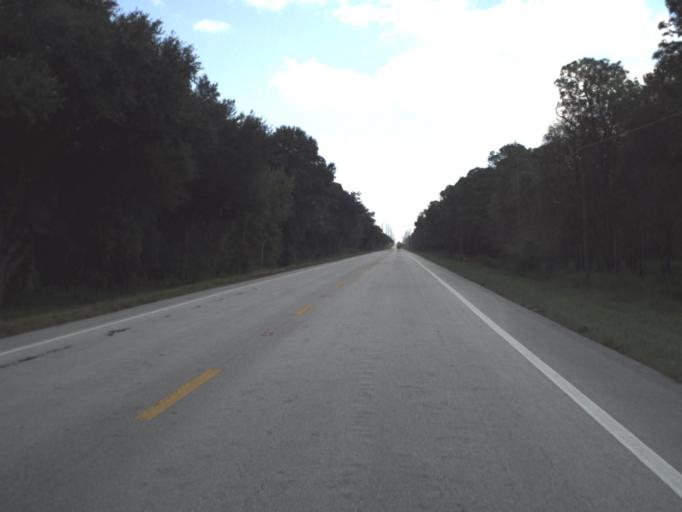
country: US
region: Florida
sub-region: Highlands County
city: Sebring
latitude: 27.4123
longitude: -81.5266
